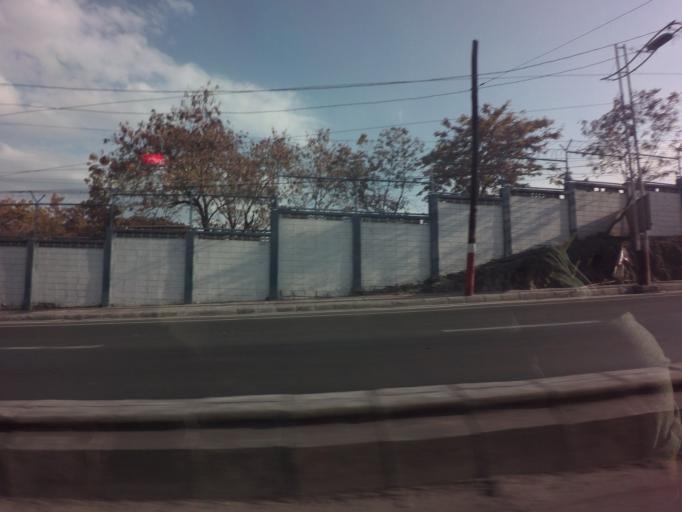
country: PH
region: Calabarzon
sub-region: Province of Rizal
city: Taguig
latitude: 14.4888
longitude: 121.0590
